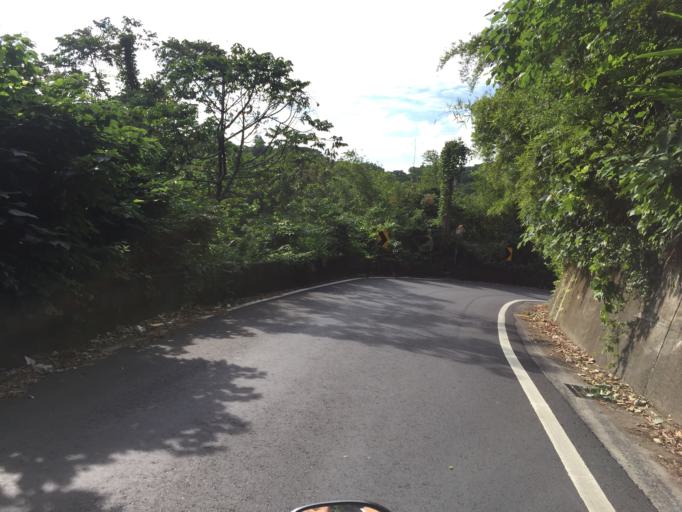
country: TW
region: Taiwan
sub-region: Hsinchu
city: Hsinchu
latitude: 24.7680
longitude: 120.9383
